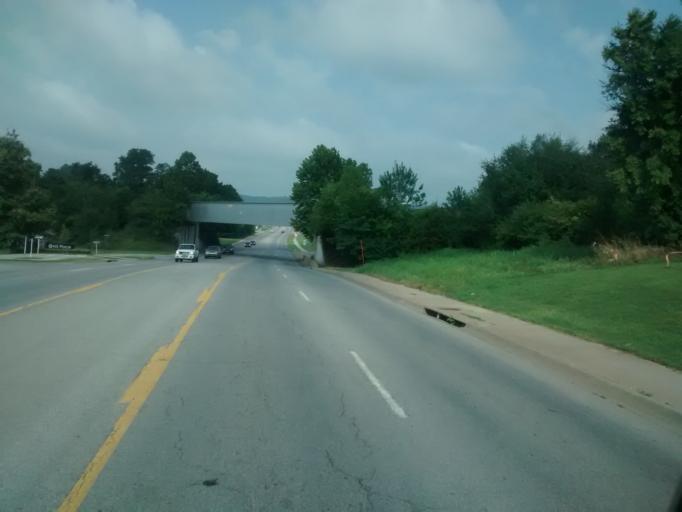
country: US
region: Arkansas
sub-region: Washington County
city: Fayetteville
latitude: 36.0567
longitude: -94.1702
